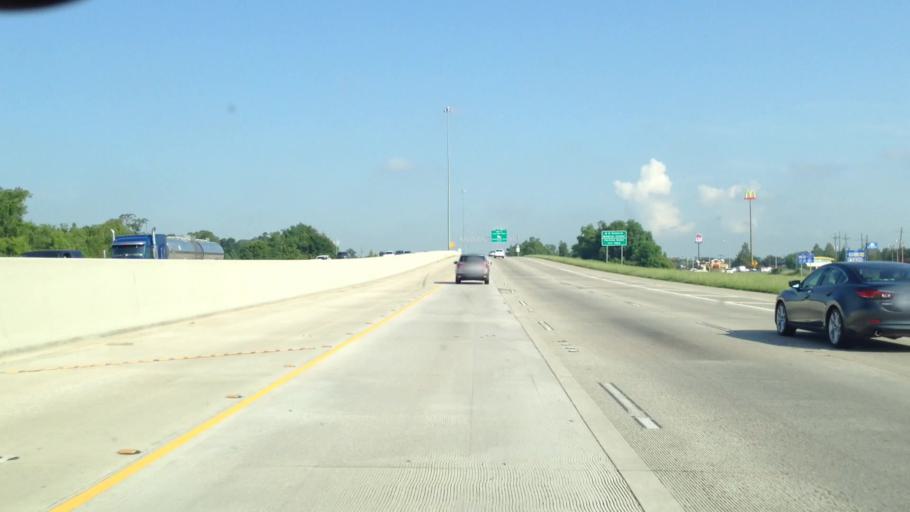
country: US
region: Louisiana
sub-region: East Baton Rouge Parish
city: Village Saint George
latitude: 30.3802
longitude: -91.0626
